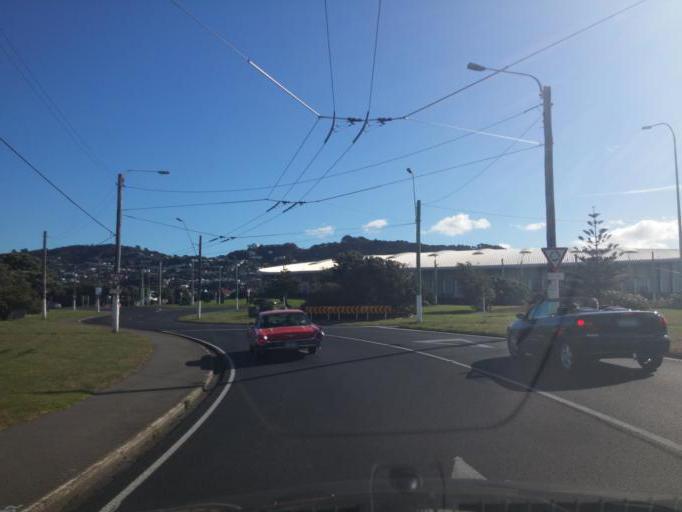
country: NZ
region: Wellington
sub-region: Wellington City
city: Wellington
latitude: -41.3173
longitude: 174.8043
